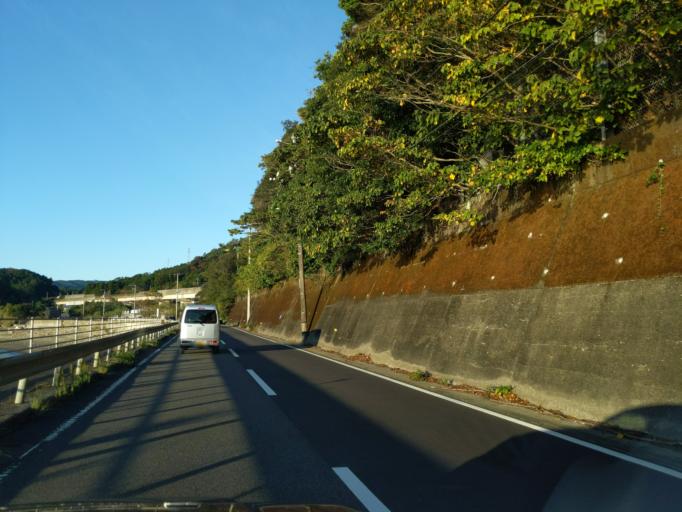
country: JP
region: Kochi
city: Muroto-misakicho
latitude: 33.5823
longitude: 134.3189
